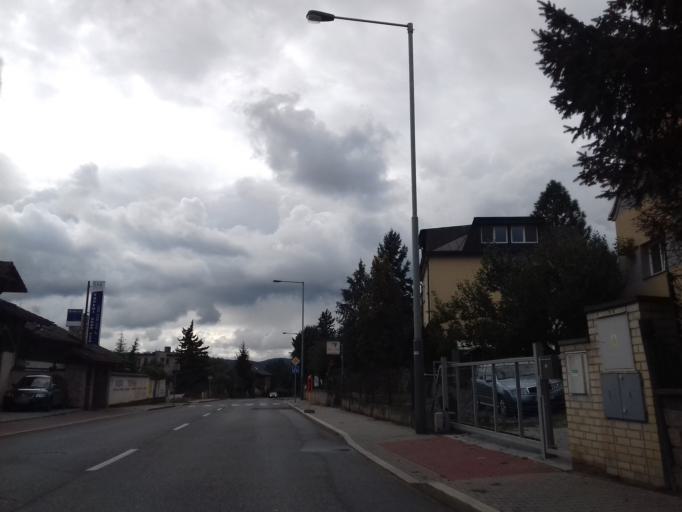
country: CZ
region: Central Bohemia
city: Cernosice
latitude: 49.9776
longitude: 14.3505
